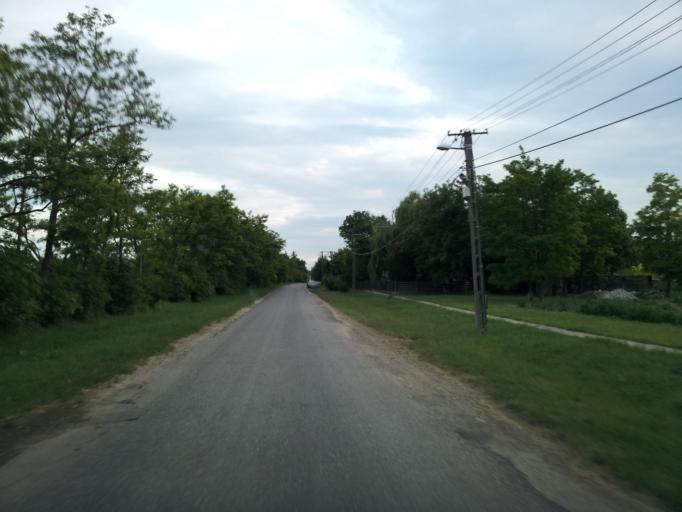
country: HU
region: Somogy
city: Balatonszabadi
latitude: 46.8846
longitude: 18.1567
